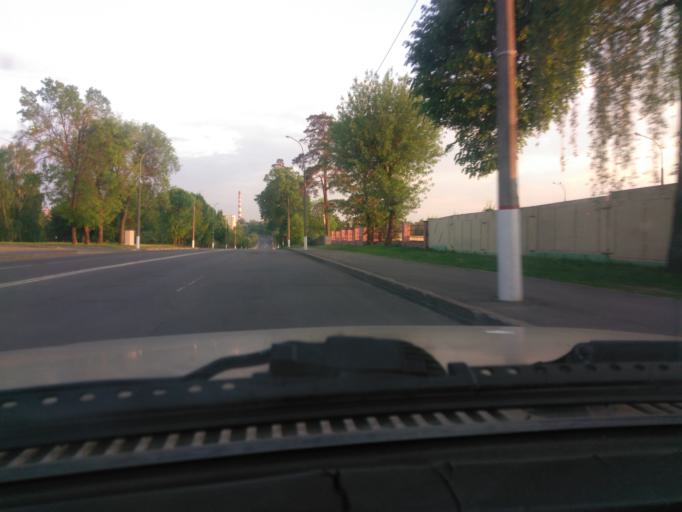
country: BY
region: Mogilev
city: Mahilyow
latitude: 53.9273
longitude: 30.3124
